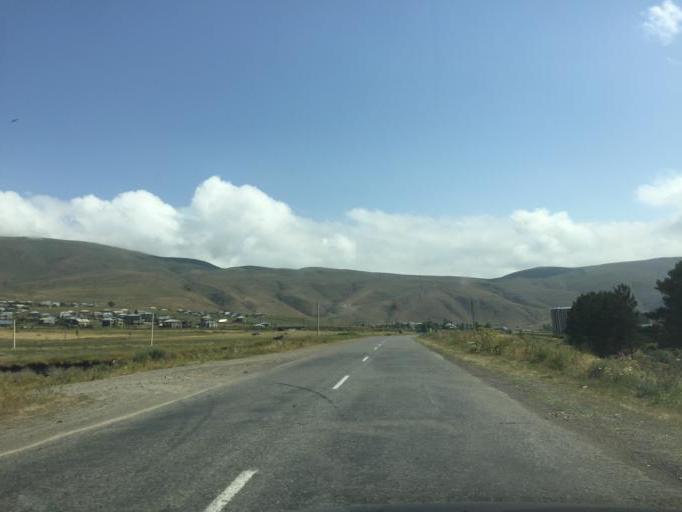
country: AM
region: Geghark'unik'i Marz
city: Tsovagyugh
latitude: 40.6191
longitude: 44.9634
